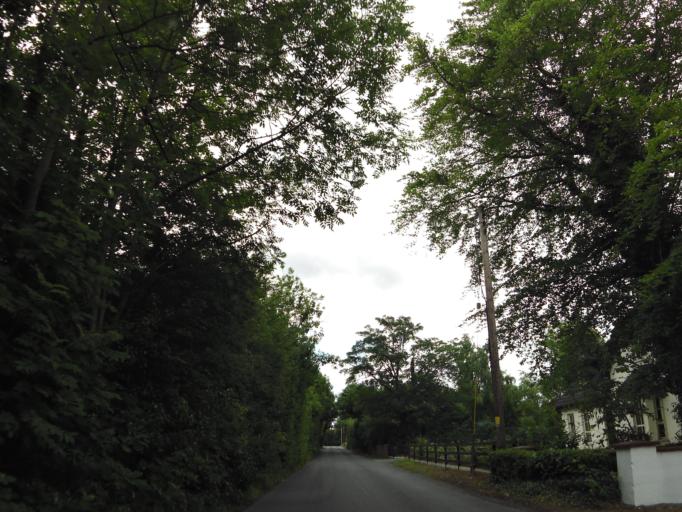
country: IE
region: Munster
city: Thurles
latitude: 52.6641
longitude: -7.7975
